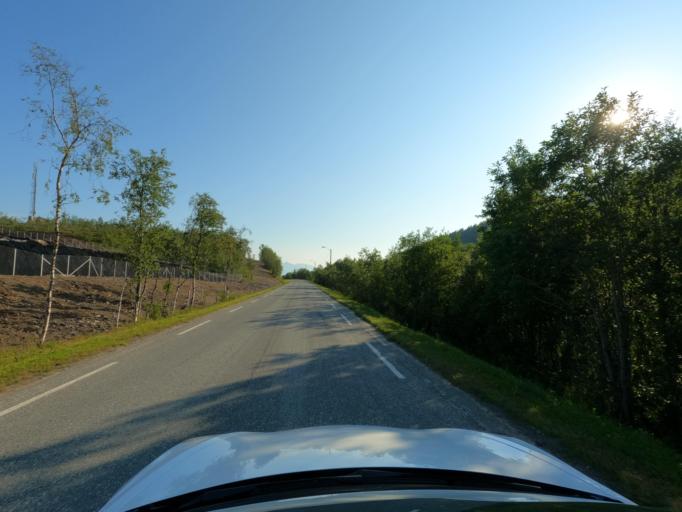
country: NO
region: Nordland
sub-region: Narvik
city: Bjerkvik
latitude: 68.5427
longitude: 17.4946
